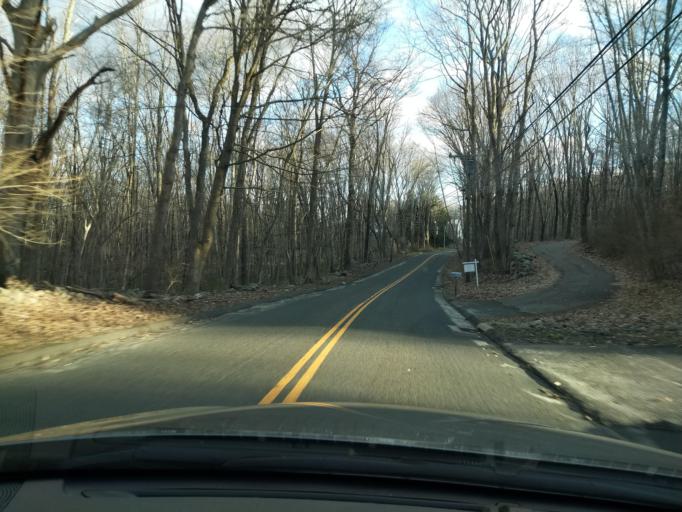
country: US
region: Connecticut
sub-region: Fairfield County
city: Newtown
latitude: 41.3747
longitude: -73.2827
